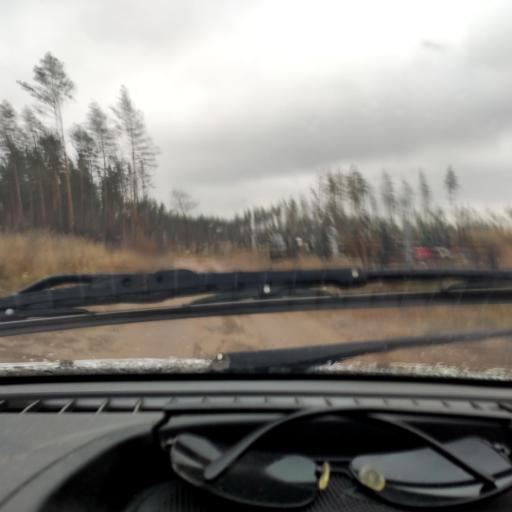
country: RU
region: Samara
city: Zhigulevsk
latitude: 53.5383
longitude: 49.5544
